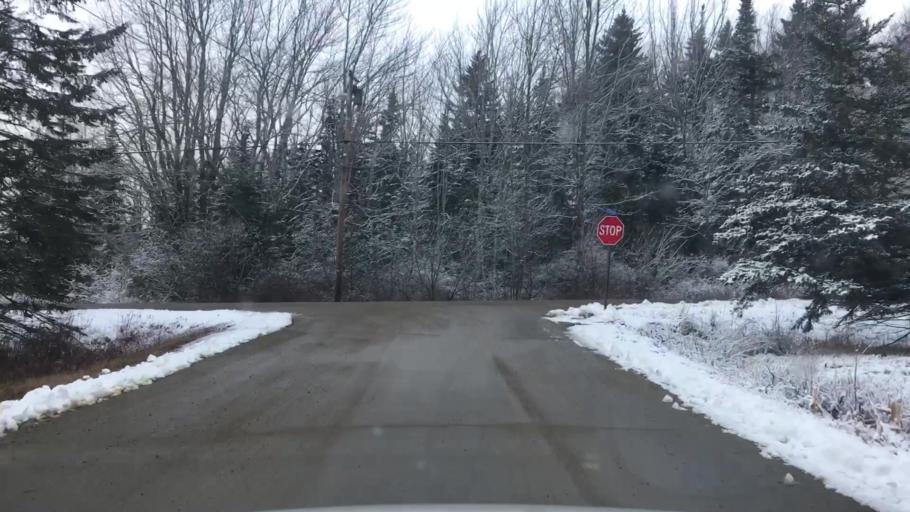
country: US
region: Maine
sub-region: Knox County
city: Owls Head
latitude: 44.0700
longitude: -69.0735
